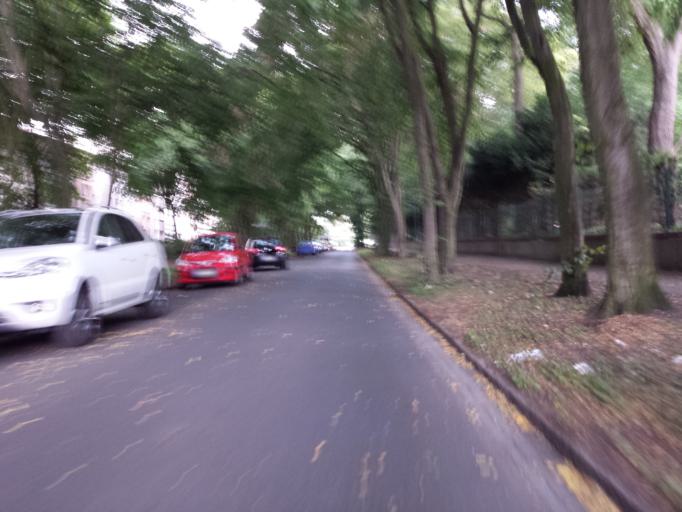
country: DE
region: Bremen
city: Bremen
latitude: 53.0852
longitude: 8.7610
